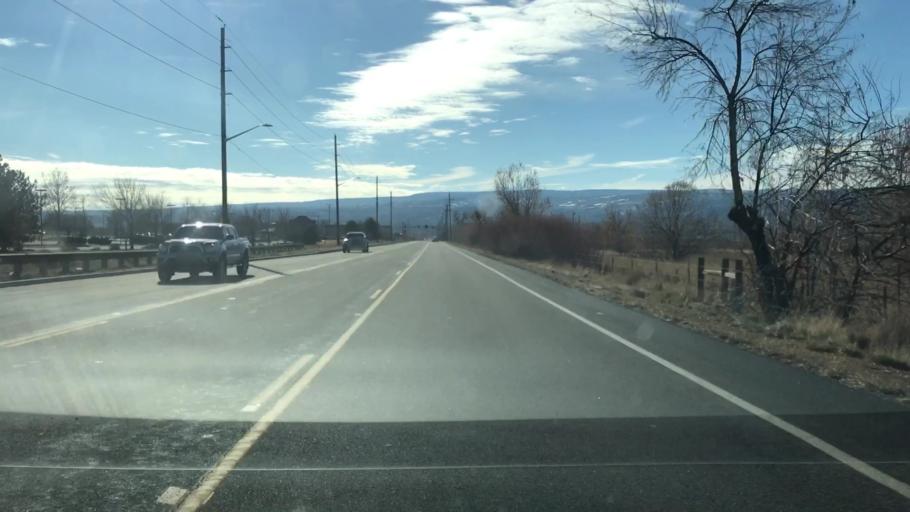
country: US
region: Colorado
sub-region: Mesa County
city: Redlands
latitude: 39.1098
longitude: -108.6082
